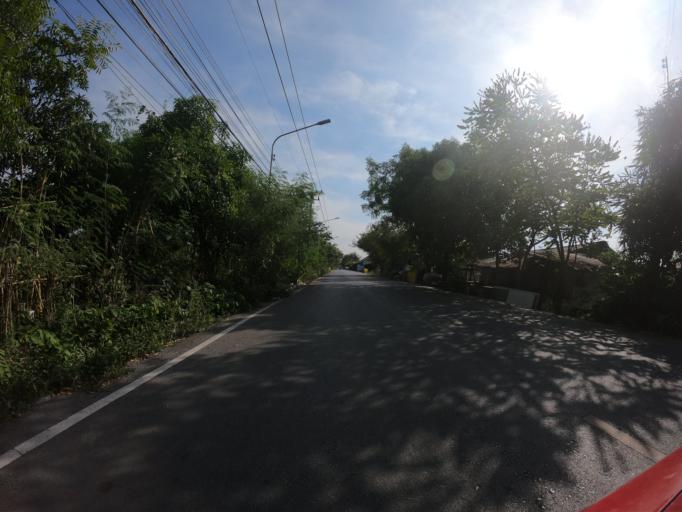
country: TH
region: Pathum Thani
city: Thanyaburi
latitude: 14.0070
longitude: 100.7314
